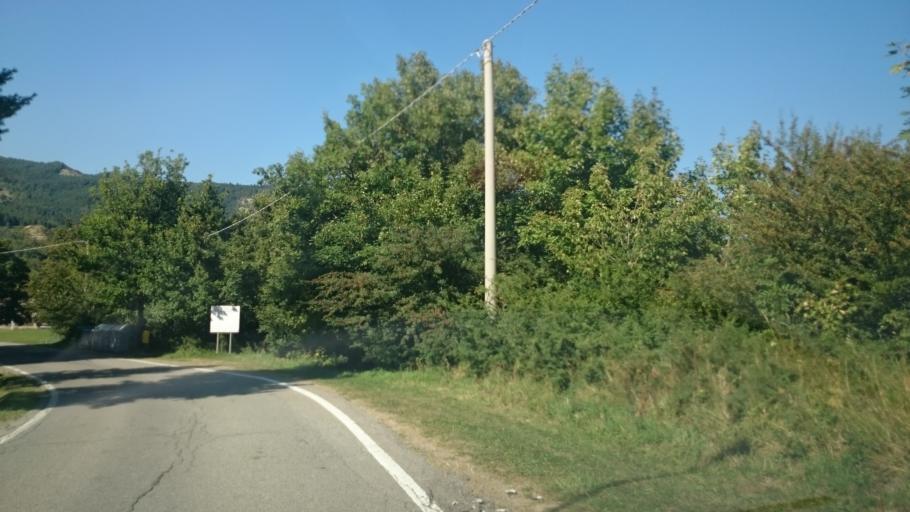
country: IT
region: Emilia-Romagna
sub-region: Provincia di Reggio Emilia
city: Villa Minozzo
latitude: 44.3040
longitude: 10.4345
